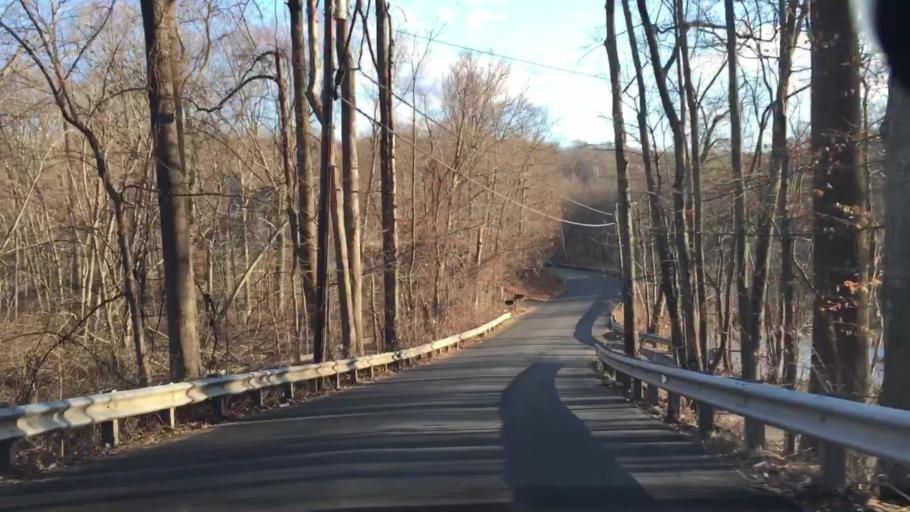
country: US
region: Connecticut
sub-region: Fairfield County
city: Newtown
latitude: 41.4418
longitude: -73.3162
